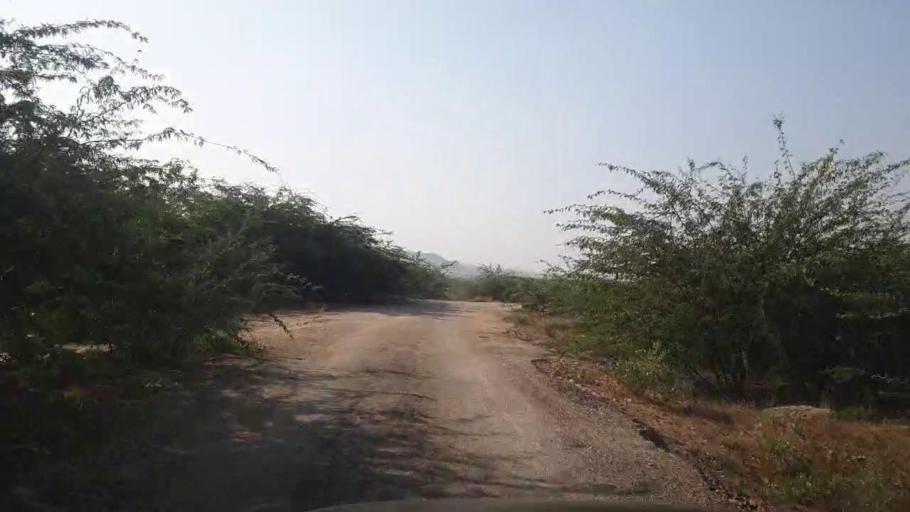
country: PK
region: Sindh
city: Gharo
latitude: 25.0517
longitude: 67.5579
